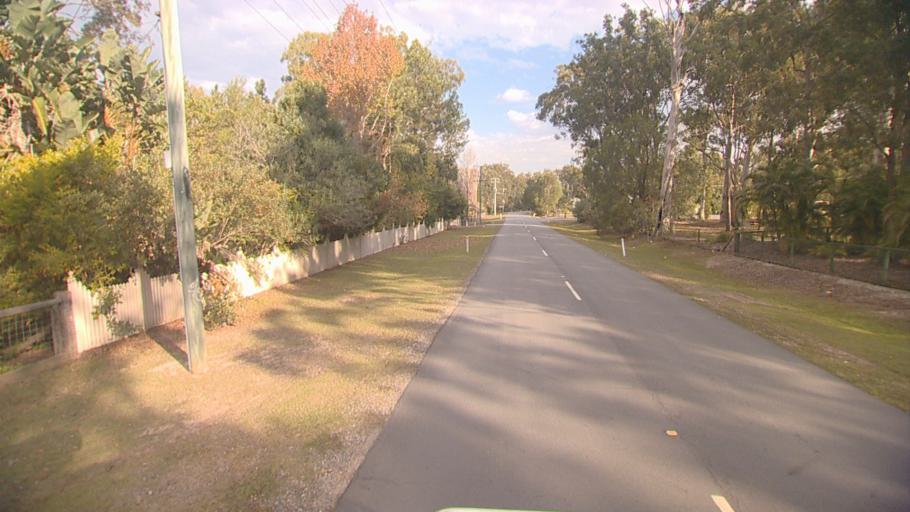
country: AU
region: Queensland
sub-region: Logan
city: Chambers Flat
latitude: -27.7808
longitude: 153.1092
